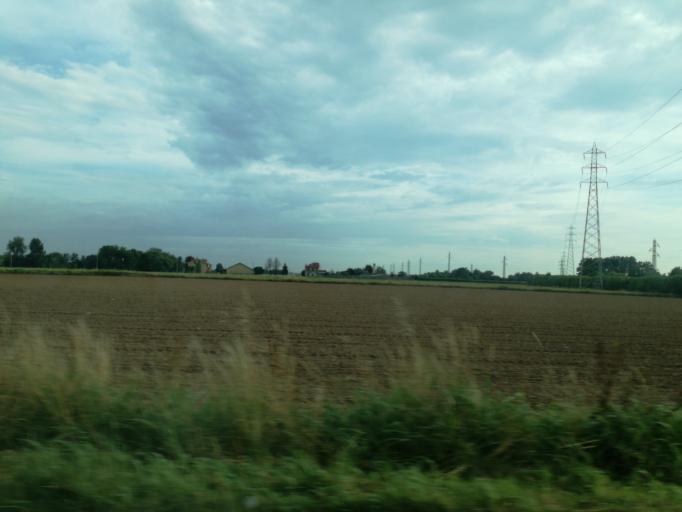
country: IT
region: Lombardy
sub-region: Provincia di Monza e Brianza
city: Velasca
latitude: 45.6222
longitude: 9.3418
